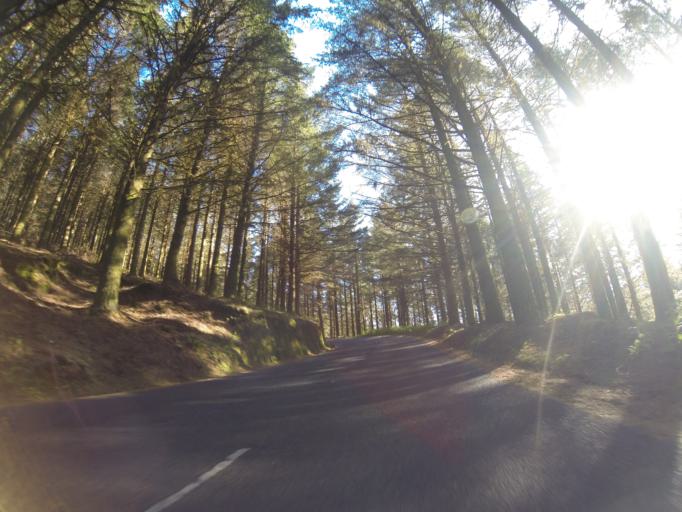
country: PT
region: Madeira
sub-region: Funchal
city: Nossa Senhora do Monte
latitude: 32.7163
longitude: -16.8859
